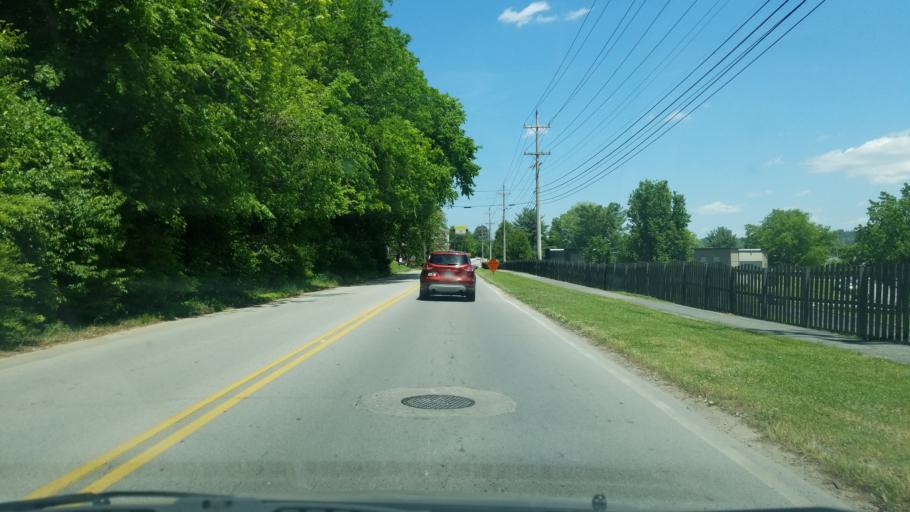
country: US
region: Tennessee
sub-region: Hamilton County
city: Signal Mountain
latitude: 35.1086
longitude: -85.3250
